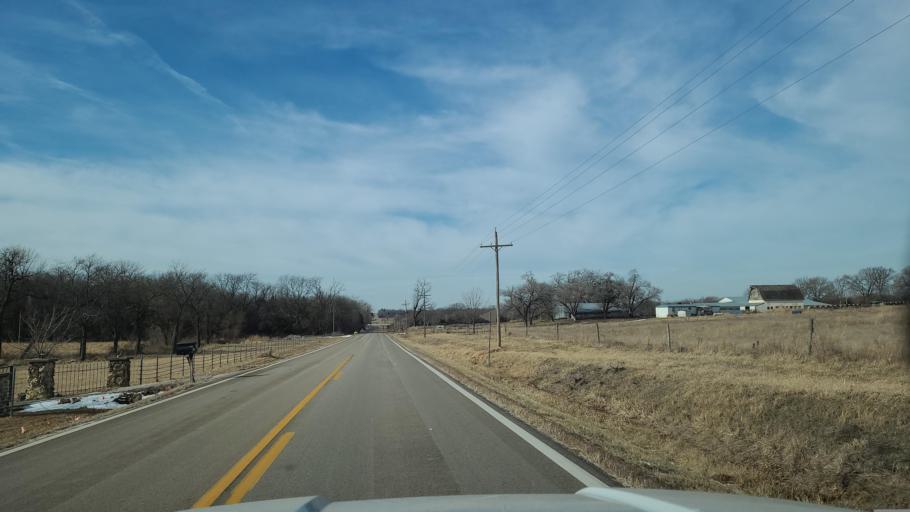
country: US
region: Kansas
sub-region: Douglas County
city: Lawrence
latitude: 38.8844
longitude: -95.1887
